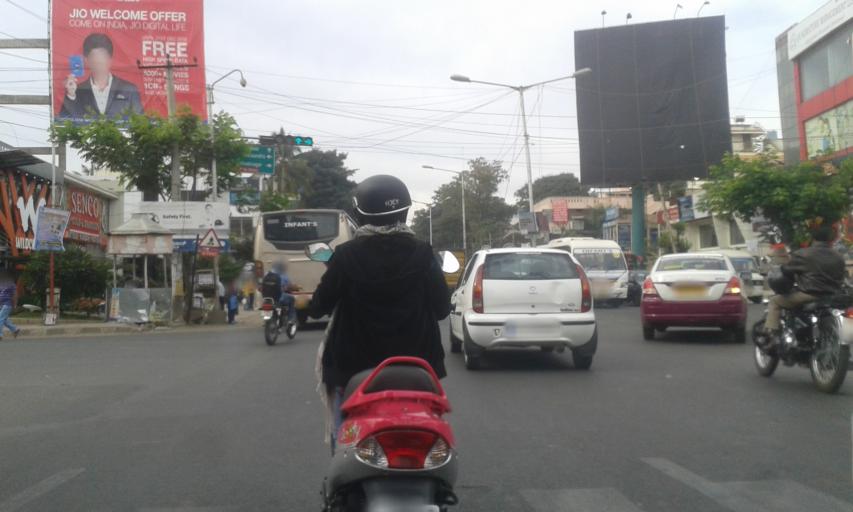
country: IN
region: Karnataka
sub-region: Bangalore Urban
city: Bangalore
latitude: 12.9373
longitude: 77.6271
